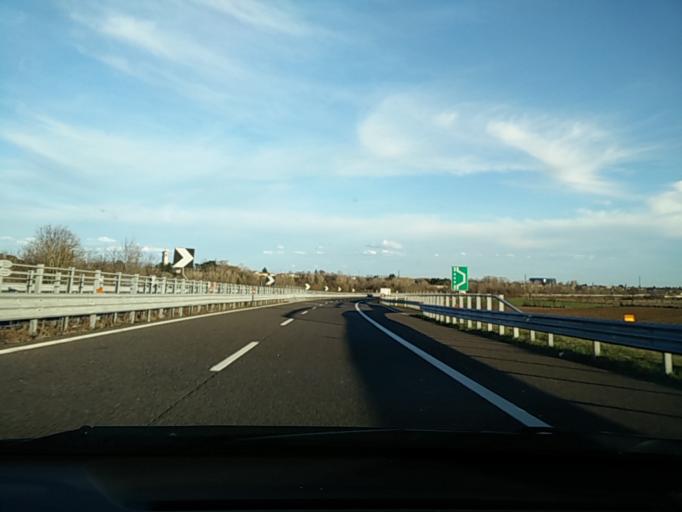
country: IT
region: Friuli Venezia Giulia
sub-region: Provincia di Udine
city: Pagnacco
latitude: 46.1285
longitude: 13.1988
